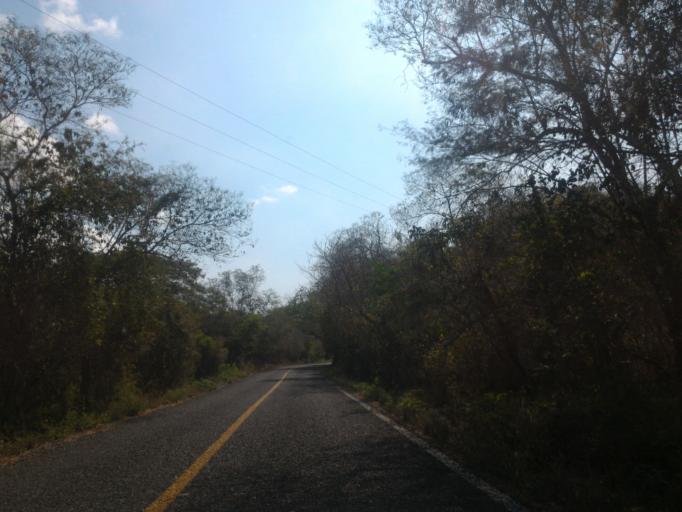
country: MX
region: Michoacan
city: Coahuayana Viejo
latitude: 18.3734
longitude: -103.5116
